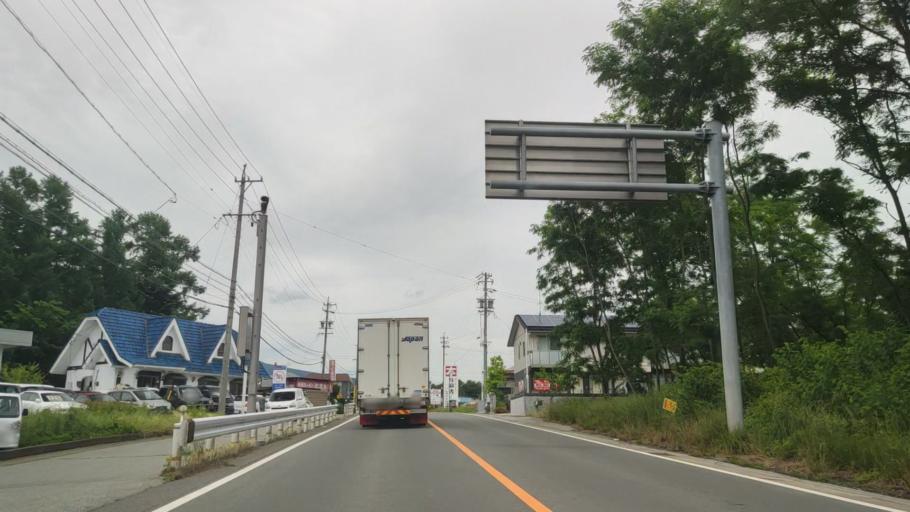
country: JP
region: Nagano
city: Komoro
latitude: 36.3232
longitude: 138.5002
